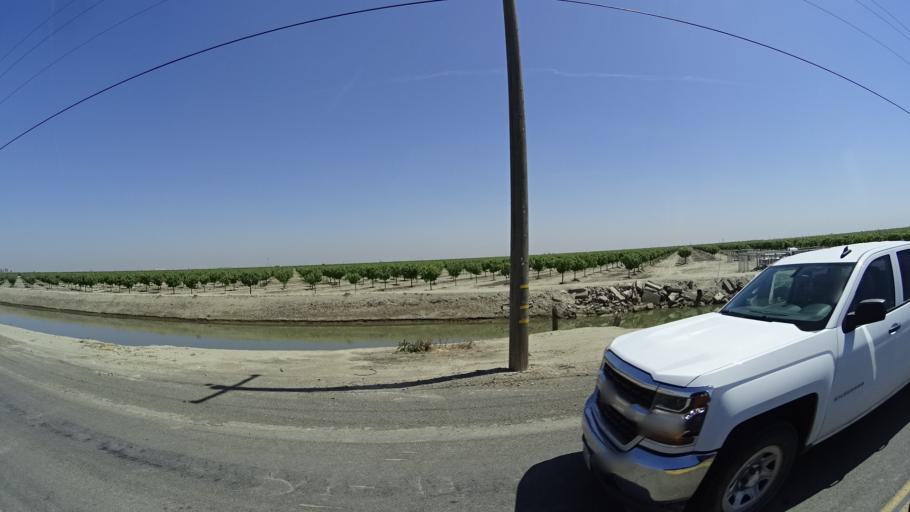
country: US
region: California
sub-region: Kings County
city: Corcoran
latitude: 36.0764
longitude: -119.5406
